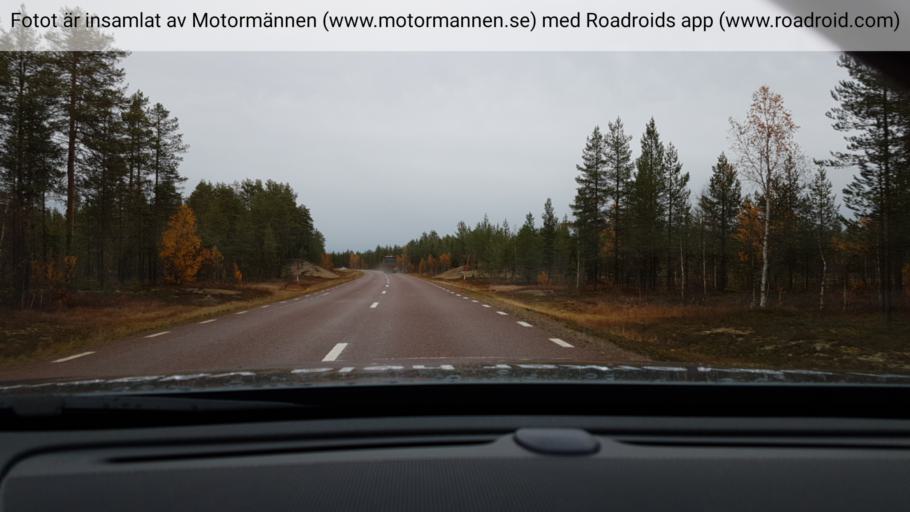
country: SE
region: Norrbotten
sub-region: Pajala Kommun
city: Pajala
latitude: 67.1716
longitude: 22.6819
